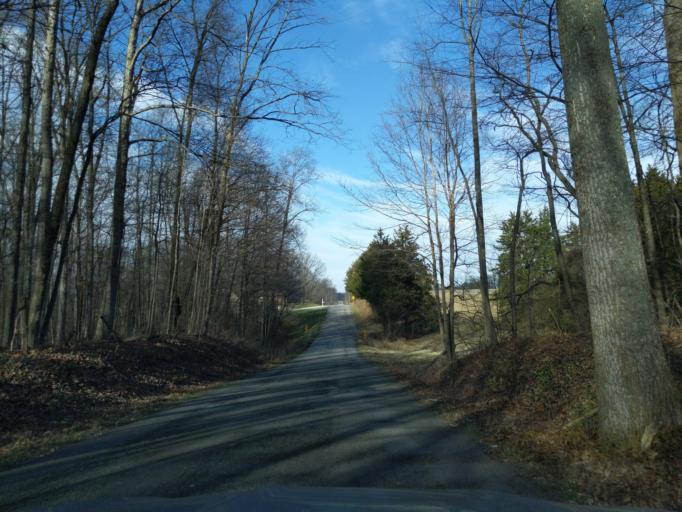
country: US
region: Indiana
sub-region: Decatur County
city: Greensburg
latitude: 39.2813
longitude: -85.4236
